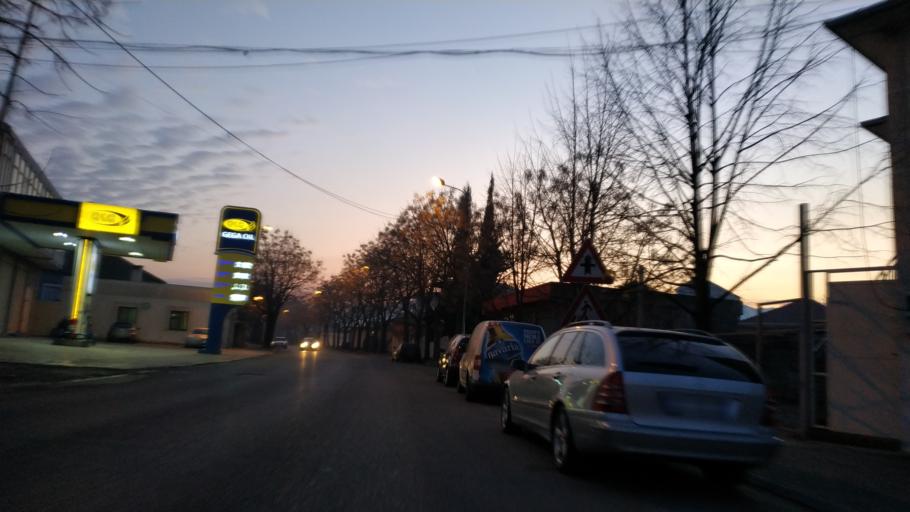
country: AL
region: Shkoder
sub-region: Rrethi i Shkodres
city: Shkoder
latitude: 42.0770
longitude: 19.5039
